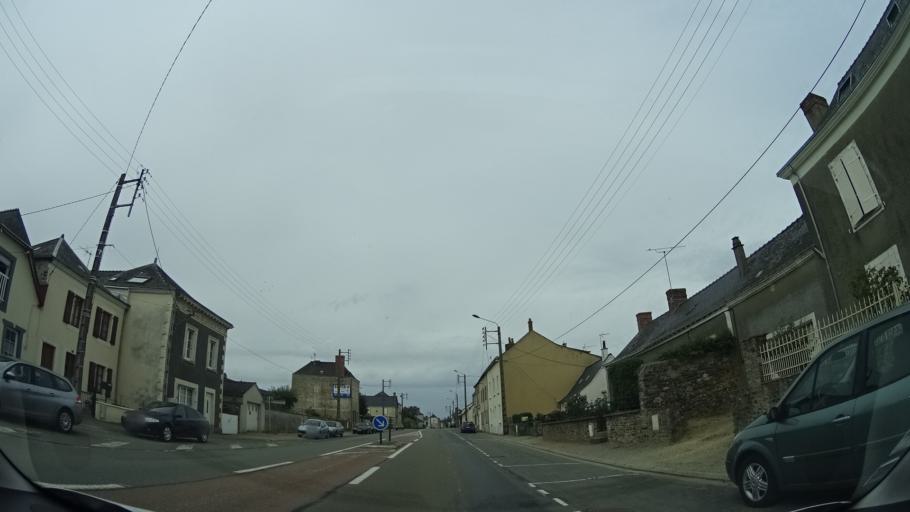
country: FR
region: Pays de la Loire
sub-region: Departement de la Mayenne
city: Meslay-du-Maine
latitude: 47.9492
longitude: -0.5461
